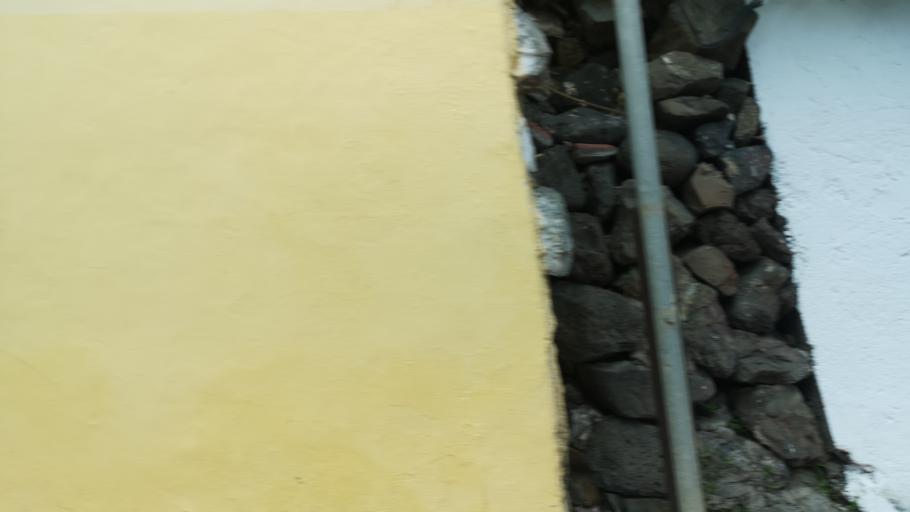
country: ES
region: Canary Islands
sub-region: Provincia de Santa Cruz de Tenerife
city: Hermigua
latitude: 28.1639
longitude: -17.1982
